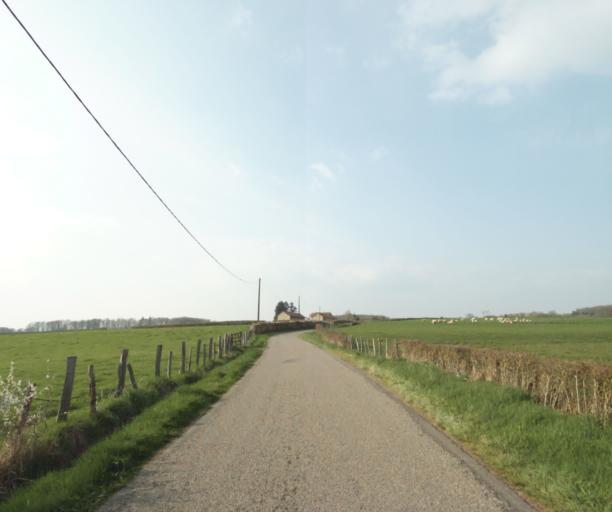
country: FR
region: Bourgogne
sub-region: Departement de Saone-et-Loire
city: Matour
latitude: 46.4693
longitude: 4.4527
